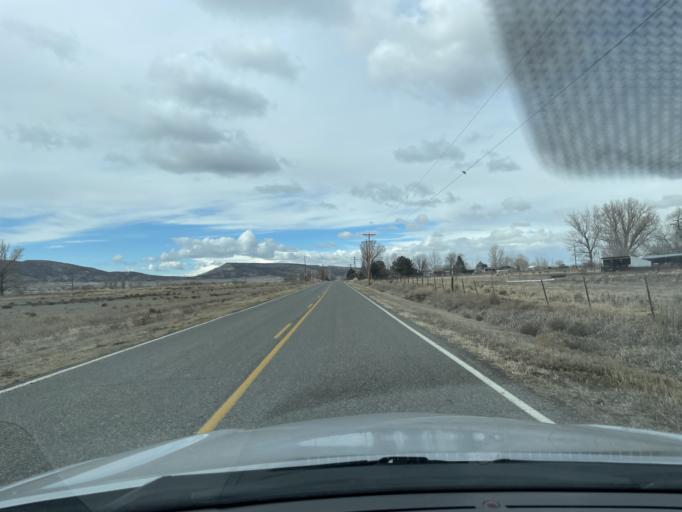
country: US
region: Colorado
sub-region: Mesa County
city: Loma
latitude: 39.2078
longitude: -108.8104
